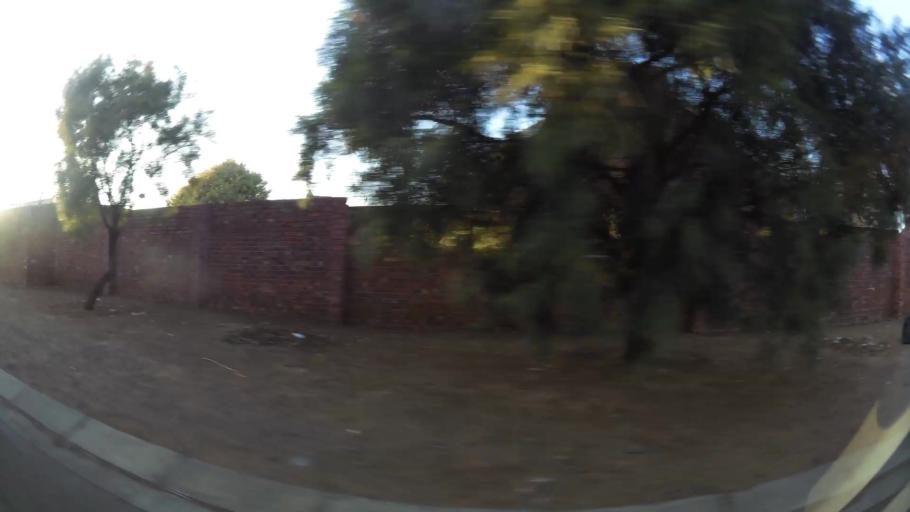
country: ZA
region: Orange Free State
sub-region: Mangaung Metropolitan Municipality
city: Bloemfontein
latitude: -29.0921
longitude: 26.1657
